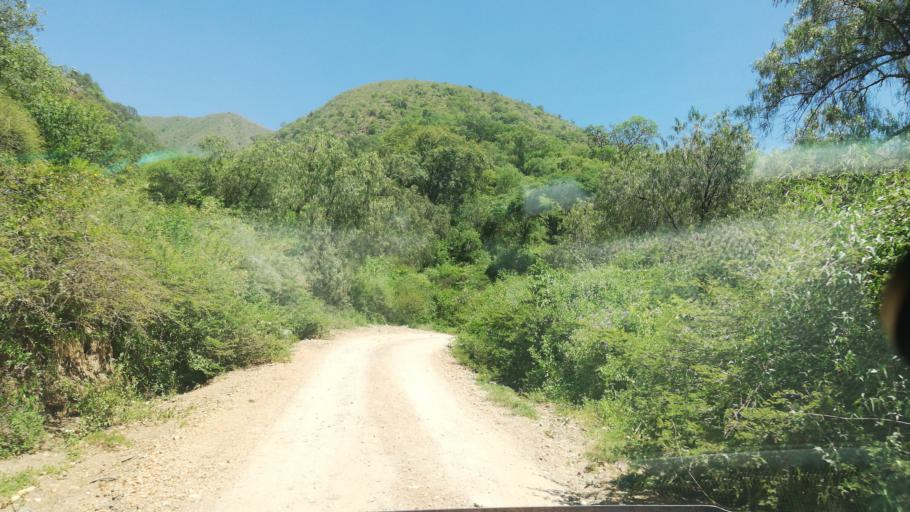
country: BO
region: Cochabamba
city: Mizque
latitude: -17.8744
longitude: -65.2939
